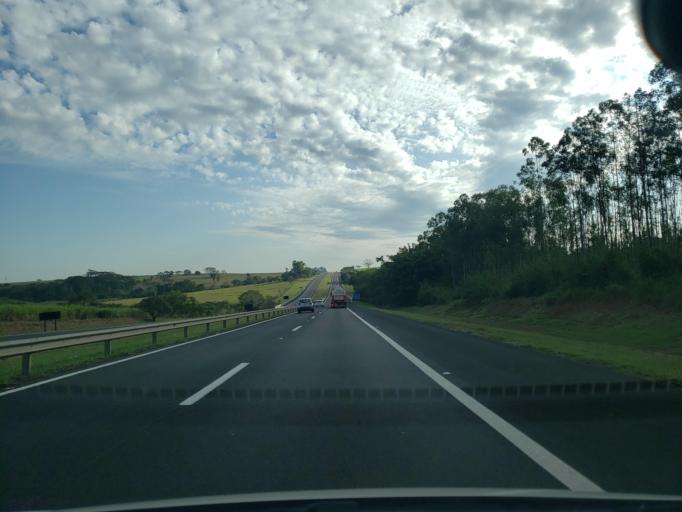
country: BR
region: Sao Paulo
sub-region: Guararapes
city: Guararapes
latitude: -21.2001
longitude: -50.5742
